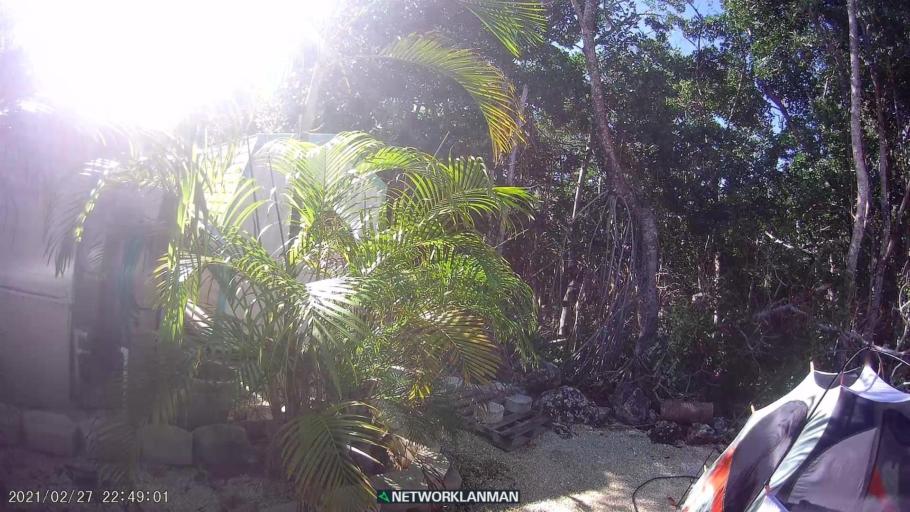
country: US
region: Florida
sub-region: Monroe County
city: Key Largo
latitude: 25.1134
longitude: -80.4167
